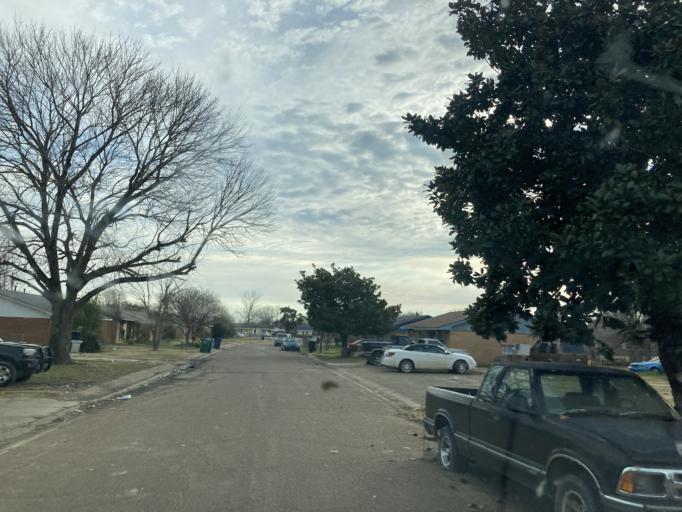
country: US
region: Mississippi
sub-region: Humphreys County
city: Belzoni
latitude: 33.1716
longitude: -90.5010
